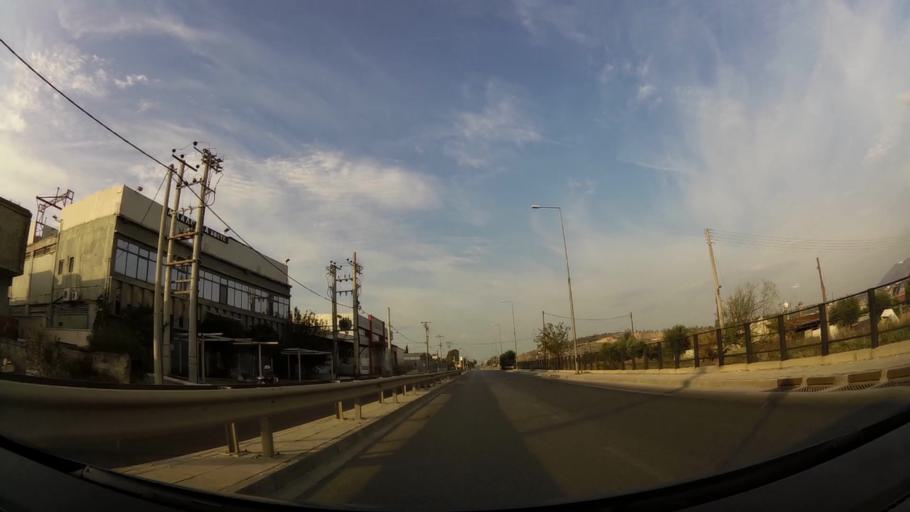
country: GR
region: Attica
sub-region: Nomarchia Dytikis Attikis
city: Ano Liosia
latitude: 38.0698
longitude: 23.6817
